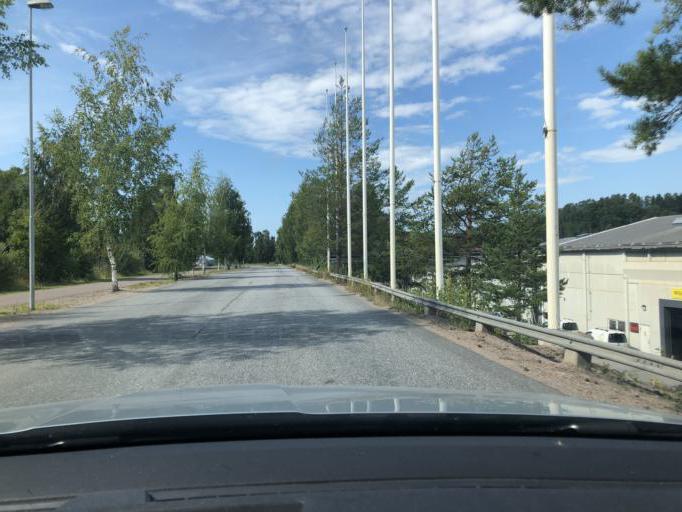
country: SE
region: Dalarna
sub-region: Avesta Kommun
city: Avesta
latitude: 60.1462
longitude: 16.1881
